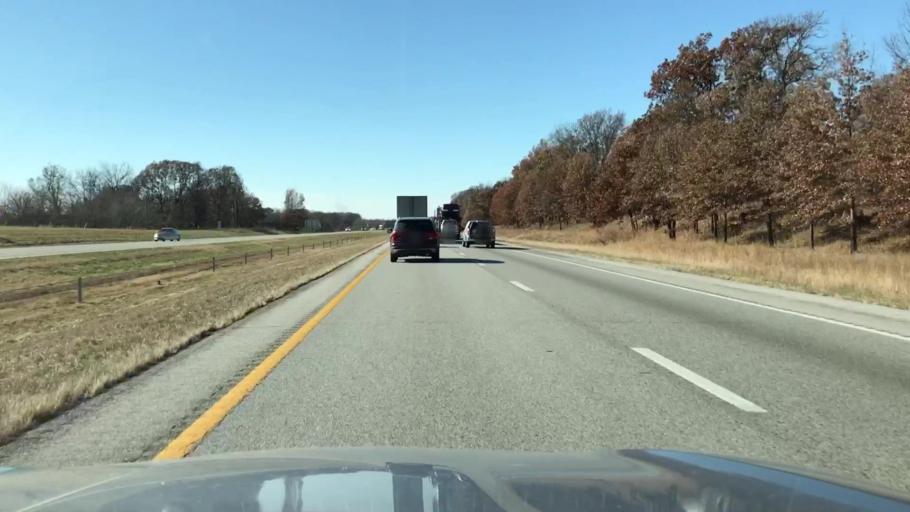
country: US
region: Missouri
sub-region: Jasper County
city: Duenweg
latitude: 37.0823
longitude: -94.3524
